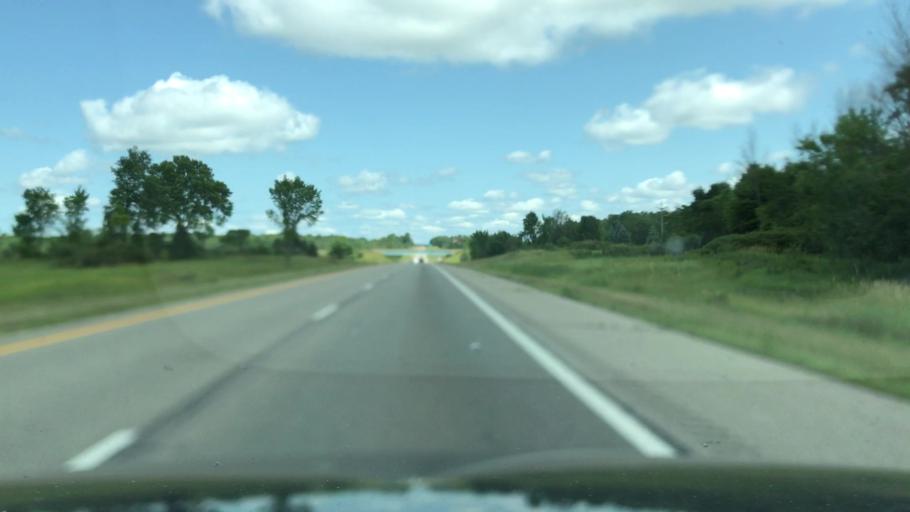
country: US
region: Michigan
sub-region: Mecosta County
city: Big Rapids
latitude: 43.7105
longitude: -85.5293
